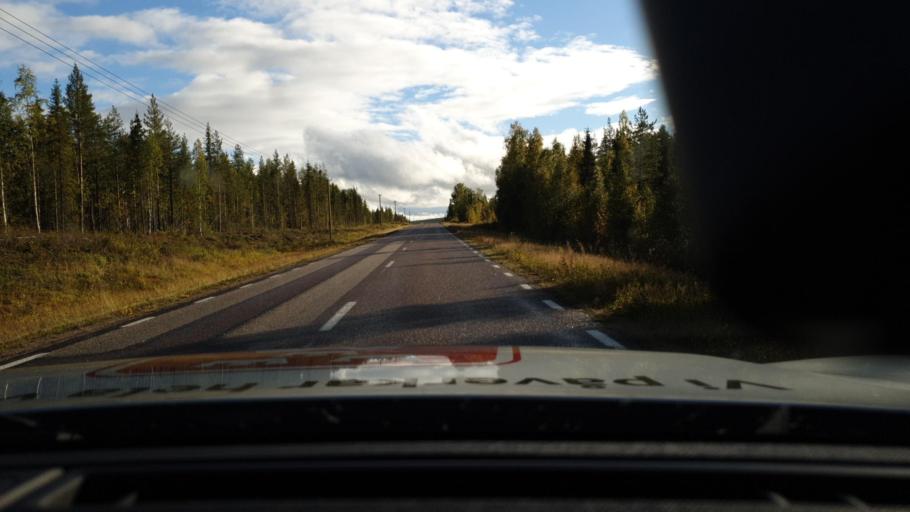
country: SE
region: Norrbotten
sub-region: Overkalix Kommun
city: OEverkalix
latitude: 66.8850
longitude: 22.7668
